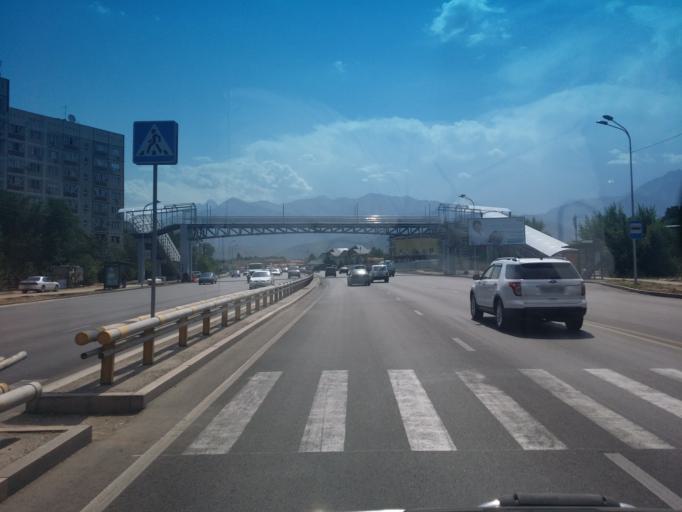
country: KZ
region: Almaty Qalasy
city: Almaty
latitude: 43.1975
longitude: 76.8715
